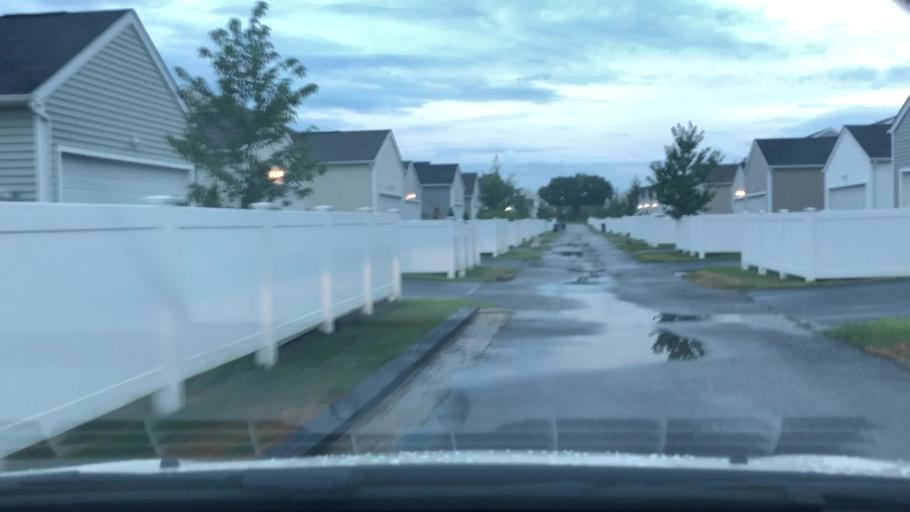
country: US
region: Ohio
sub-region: Franklin County
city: New Albany
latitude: 40.0980
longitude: -82.8528
